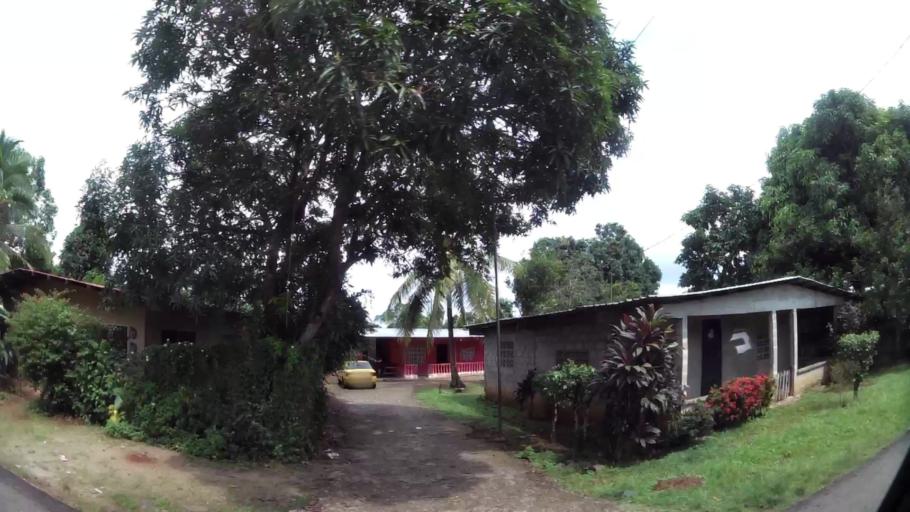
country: PA
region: Panama
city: Cabra Numero Uno
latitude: 9.1103
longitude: -79.3280
